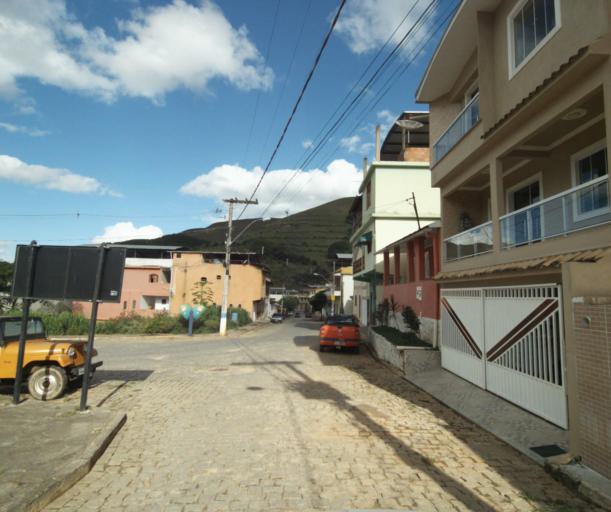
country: BR
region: Espirito Santo
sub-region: Irupi
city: Irupi
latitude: -20.5404
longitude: -41.6681
